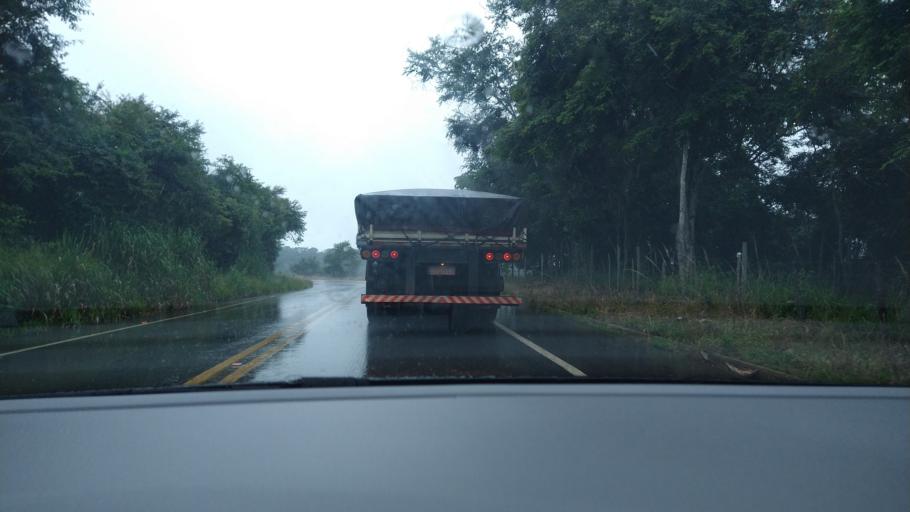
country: BR
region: Minas Gerais
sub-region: Ponte Nova
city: Ponte Nova
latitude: -20.5765
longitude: -42.8777
